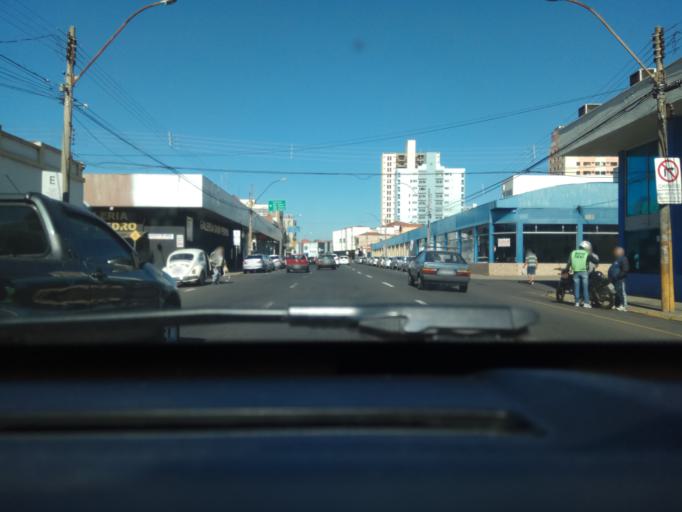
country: BR
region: Sao Paulo
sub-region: Piracicaba
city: Piracicaba
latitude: -22.7287
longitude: -47.6477
